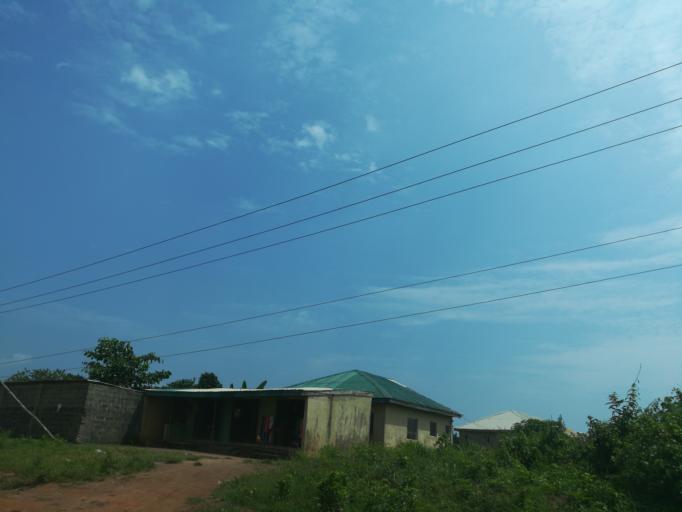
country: NG
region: Lagos
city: Ikorodu
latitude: 6.5919
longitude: 3.6433
